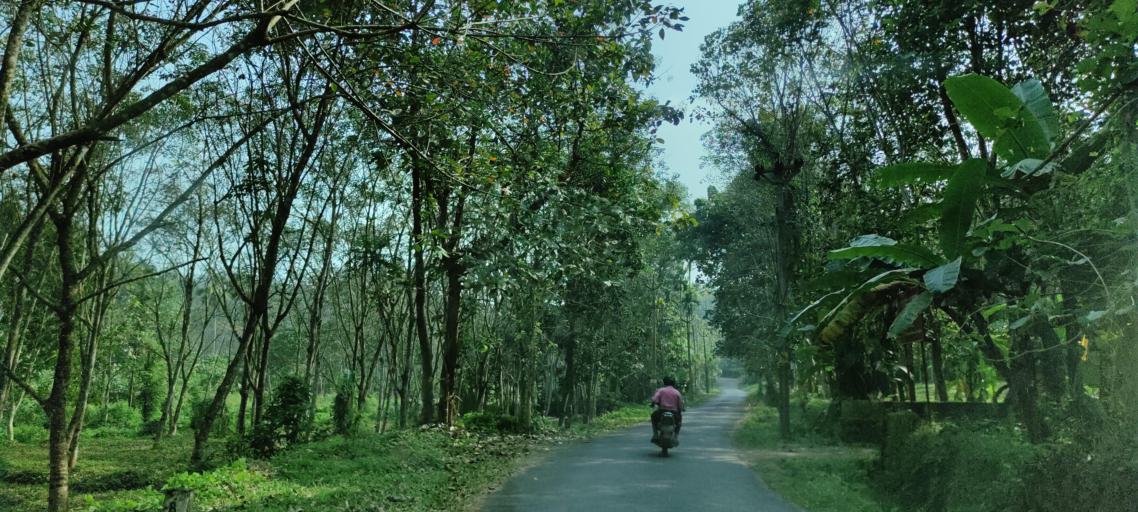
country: IN
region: Kerala
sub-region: Ernakulam
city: Piravam
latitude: 9.8111
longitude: 76.5250
